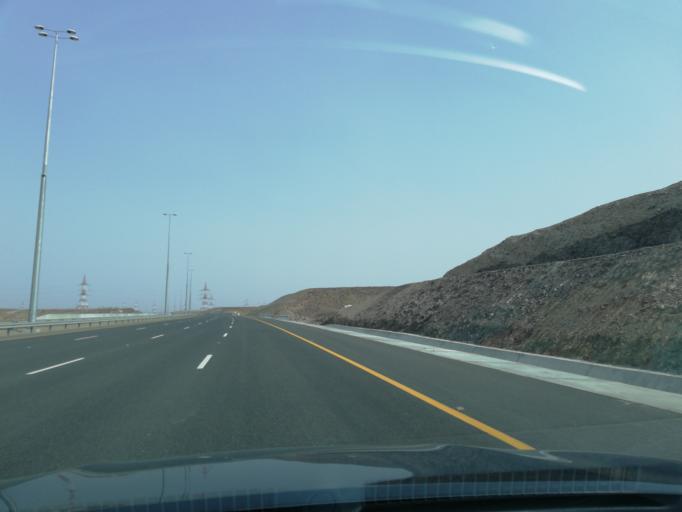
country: OM
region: Al Batinah
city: Al Sohar
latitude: 24.3399
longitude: 56.5519
